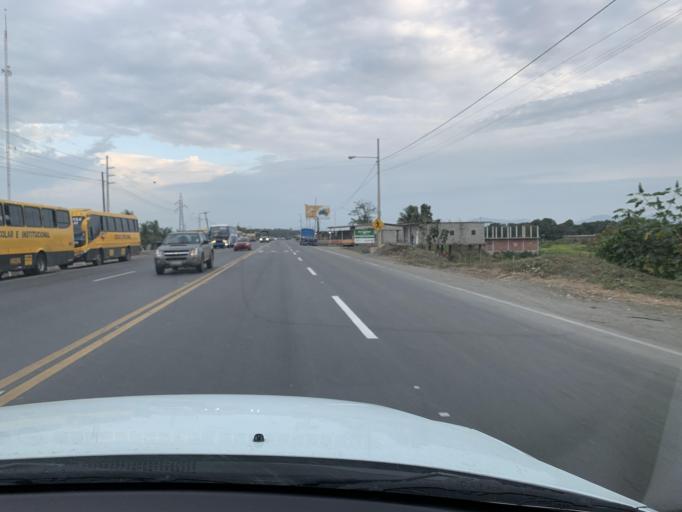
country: EC
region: Guayas
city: Yaguachi Nuevo
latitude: -2.2418
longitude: -79.6376
